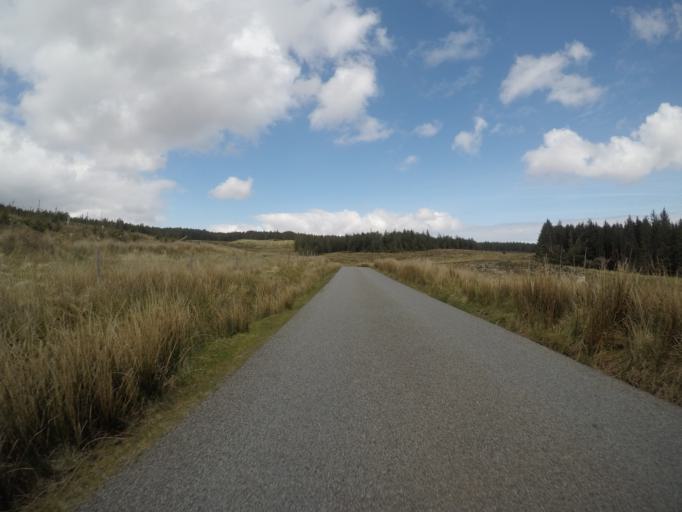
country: GB
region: Scotland
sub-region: Highland
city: Isle of Skye
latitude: 57.4080
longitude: -6.3159
